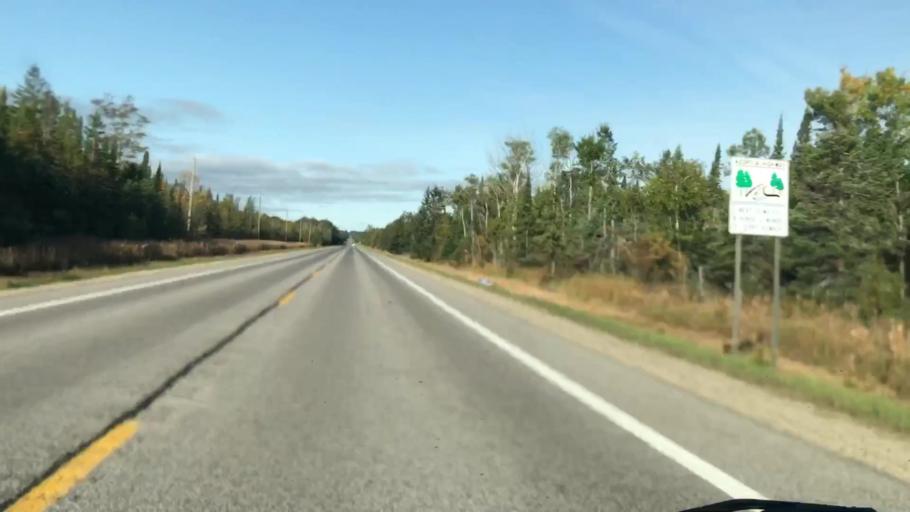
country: US
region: Michigan
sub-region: Luce County
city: Newberry
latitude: 46.3034
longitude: -85.3792
